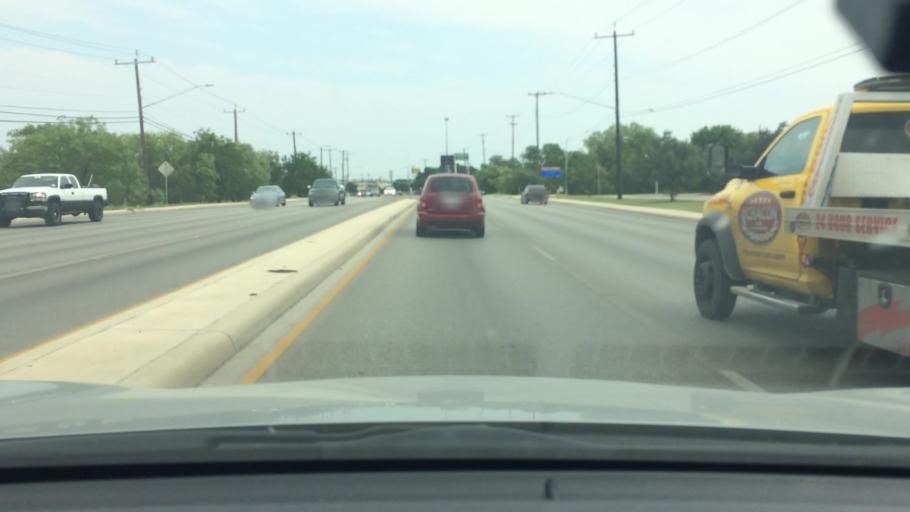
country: US
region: Texas
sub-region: Bexar County
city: Leon Valley
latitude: 29.4722
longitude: -98.6523
